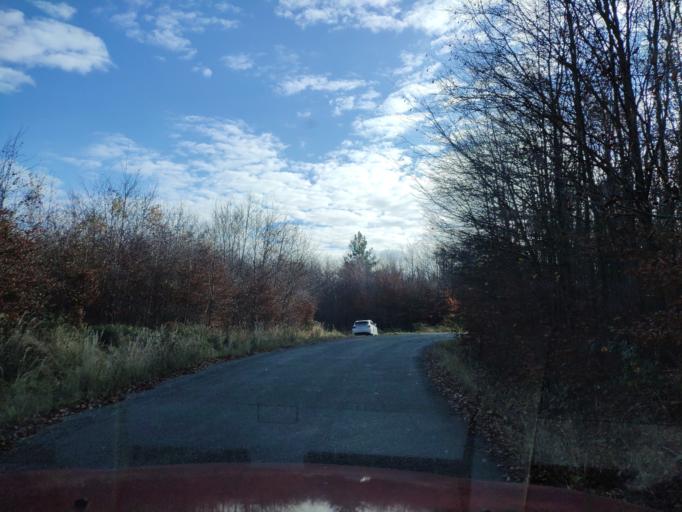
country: SK
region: Kosicky
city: Secovce
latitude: 48.6253
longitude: 21.4614
